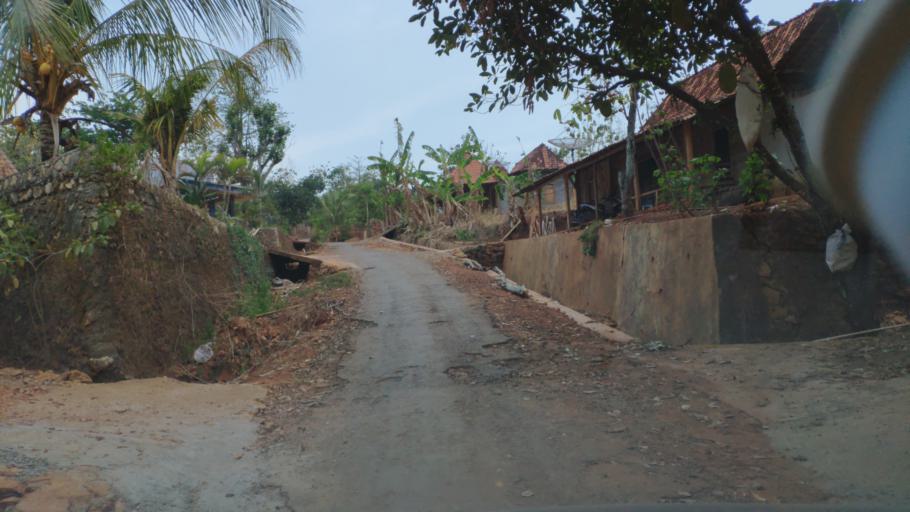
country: ID
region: Central Java
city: Guyangan
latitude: -6.9197
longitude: 111.1226
